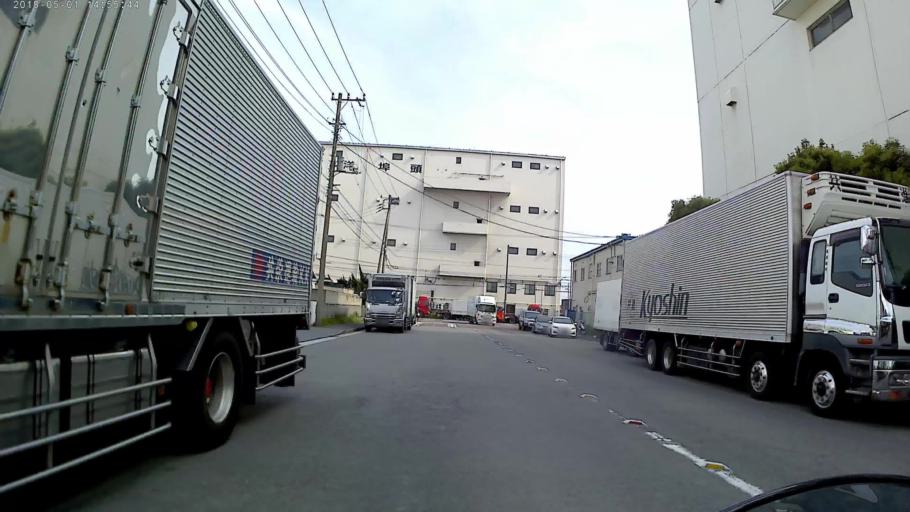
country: JP
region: Kanagawa
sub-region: Kawasaki-shi
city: Kawasaki
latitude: 35.4955
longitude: 139.7615
